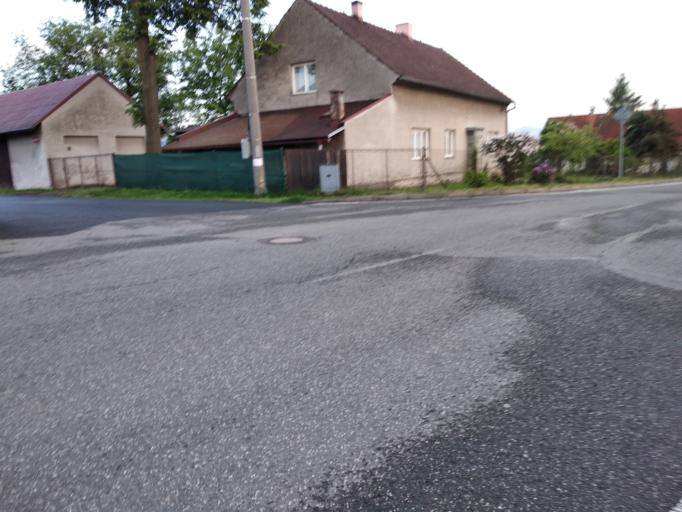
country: CZ
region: Moravskoslezsky
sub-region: Okres Frydek-Mistek
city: Stare Mesto
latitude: 49.6883
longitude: 18.3716
